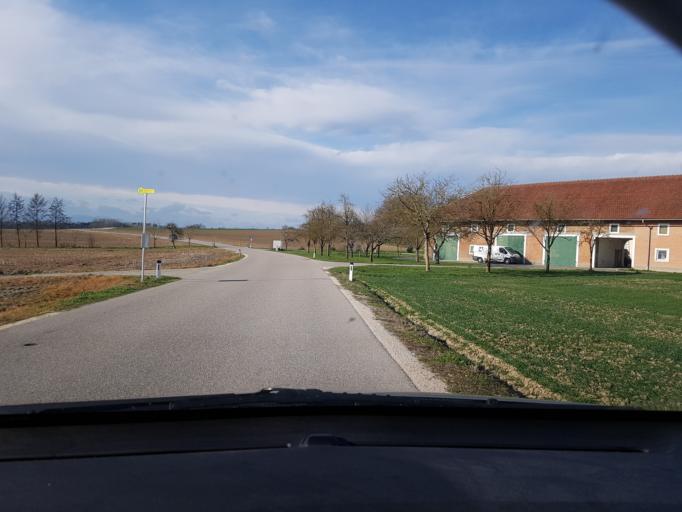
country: AT
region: Upper Austria
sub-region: Politischer Bezirk Linz-Land
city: Sankt Florian
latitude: 48.1711
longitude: 14.4075
